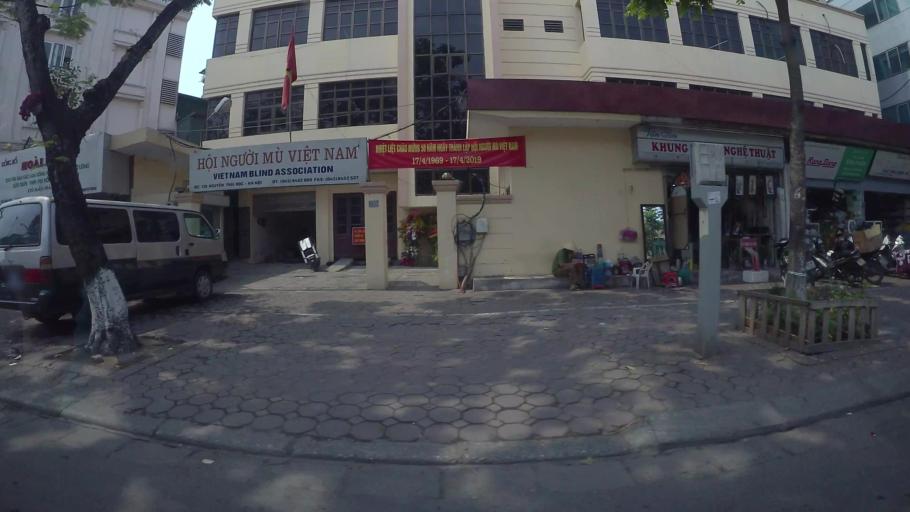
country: VN
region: Ha Noi
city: Hanoi
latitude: 21.0306
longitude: 105.8353
